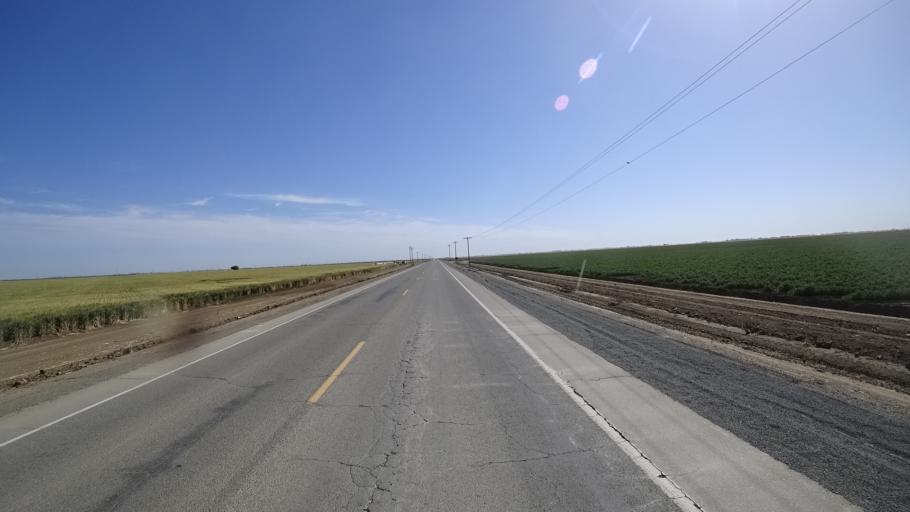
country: US
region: California
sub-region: Kings County
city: Lemoore Station
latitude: 36.2051
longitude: -119.9253
